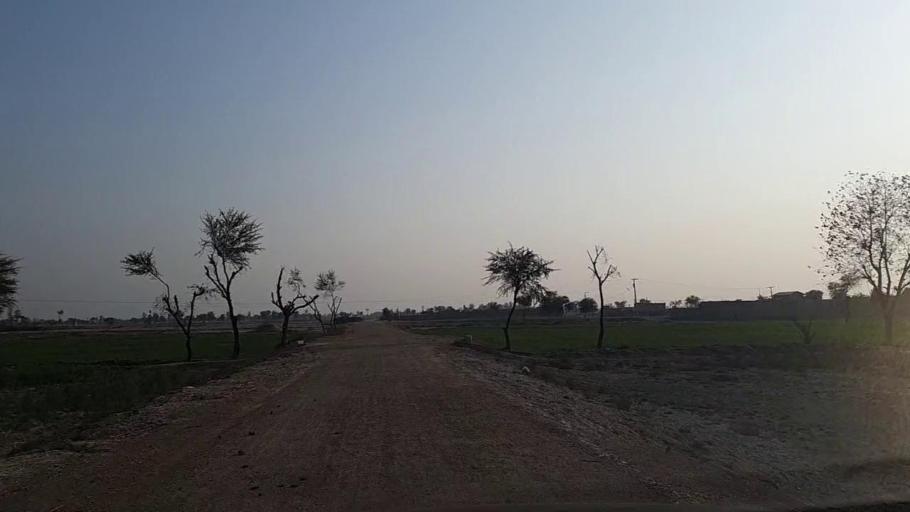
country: PK
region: Sindh
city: Daur
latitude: 26.3958
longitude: 68.3917
